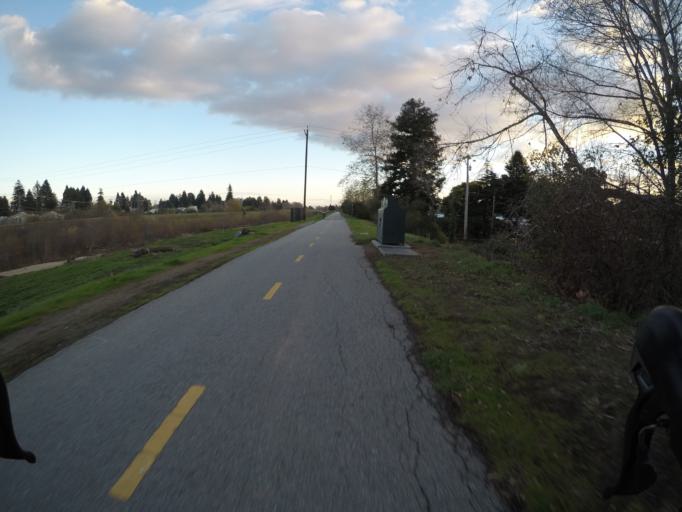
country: US
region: California
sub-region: Santa Cruz County
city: Santa Cruz
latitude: 36.9823
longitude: -122.0271
